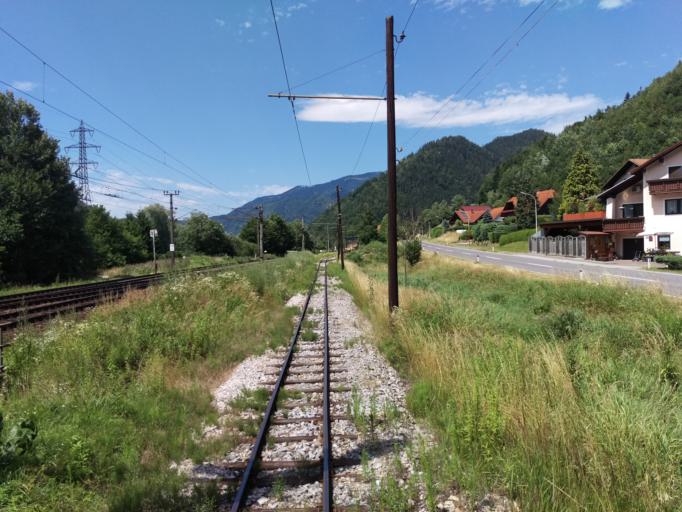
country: AT
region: Styria
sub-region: Politischer Bezirk Graz-Umgebung
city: Rothelstein
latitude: 47.3371
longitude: 15.3562
